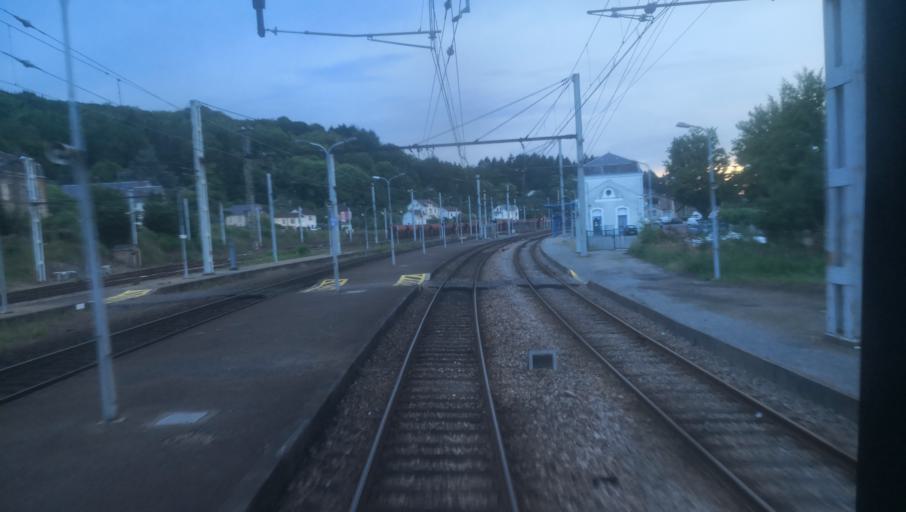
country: FR
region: Limousin
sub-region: Departement de la Haute-Vienne
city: Ambazac
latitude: 46.0462
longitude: 1.4778
